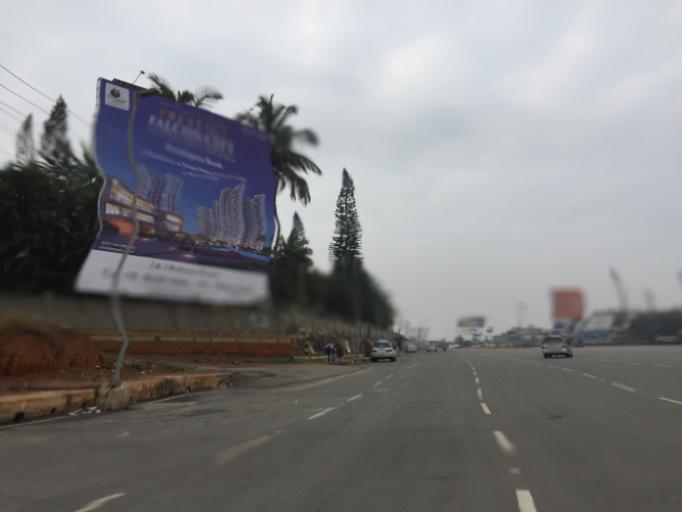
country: IN
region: Karnataka
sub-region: Bangalore Rural
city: Devanhalli
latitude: 13.1919
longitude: 77.6482
